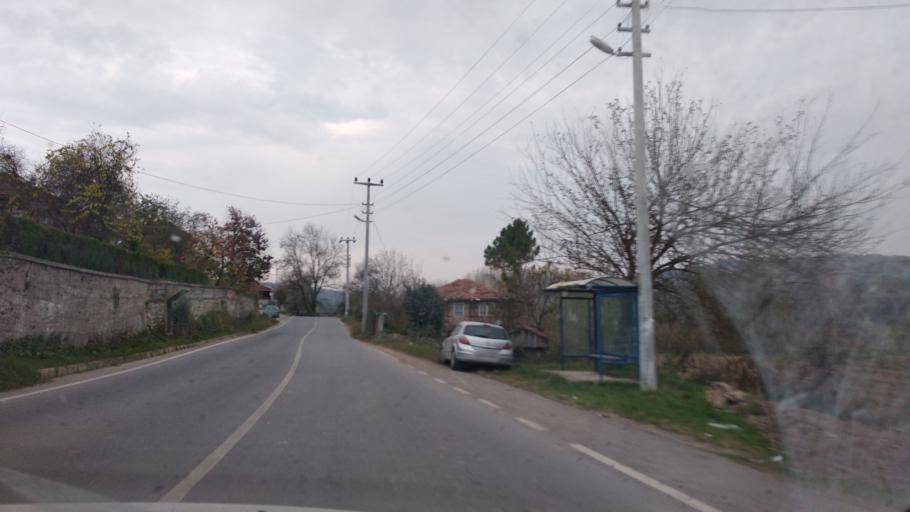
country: TR
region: Sakarya
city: Ortakoy
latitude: 41.0399
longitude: 30.6422
